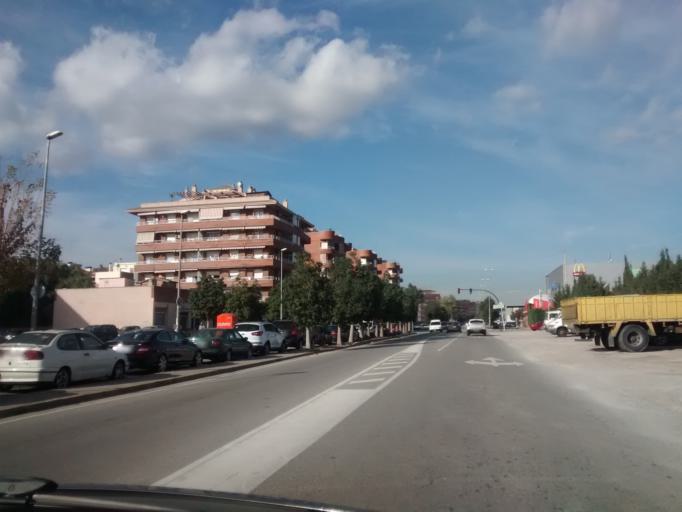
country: ES
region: Catalonia
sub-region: Provincia de Barcelona
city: Sant Vicenc dels Horts
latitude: 41.3953
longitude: 2.0117
